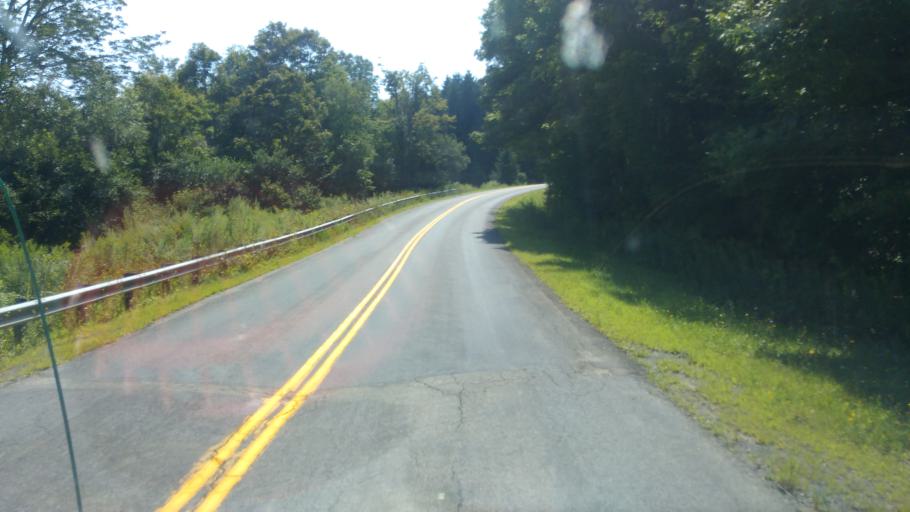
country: US
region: New York
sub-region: Steuben County
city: Canisteo
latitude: 42.3539
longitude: -77.5488
